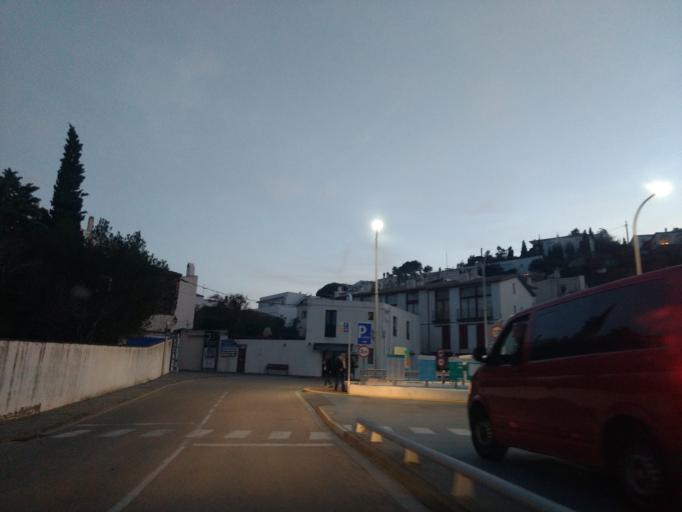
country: ES
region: Catalonia
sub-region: Provincia de Girona
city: Cadaques
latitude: 42.2892
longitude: 3.2742
